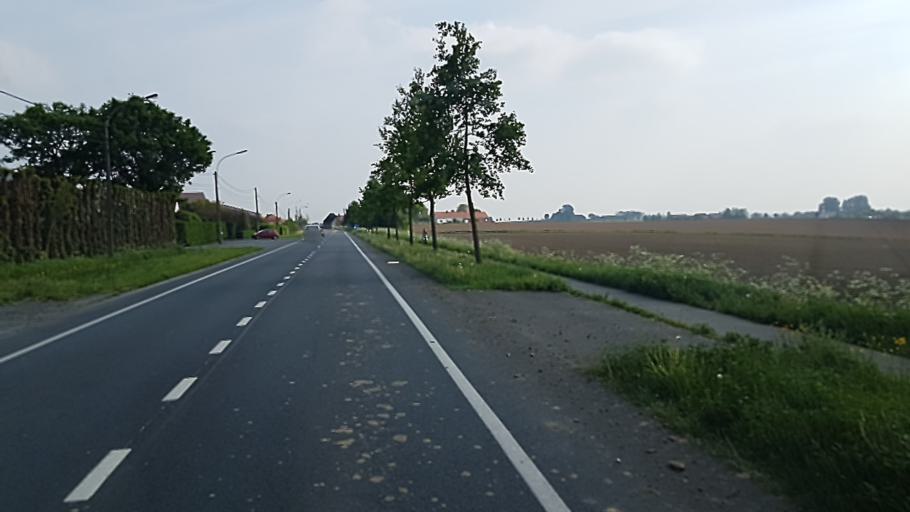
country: BE
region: Flanders
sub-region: Provincie West-Vlaanderen
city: Zwevegem
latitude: 50.7608
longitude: 3.3108
